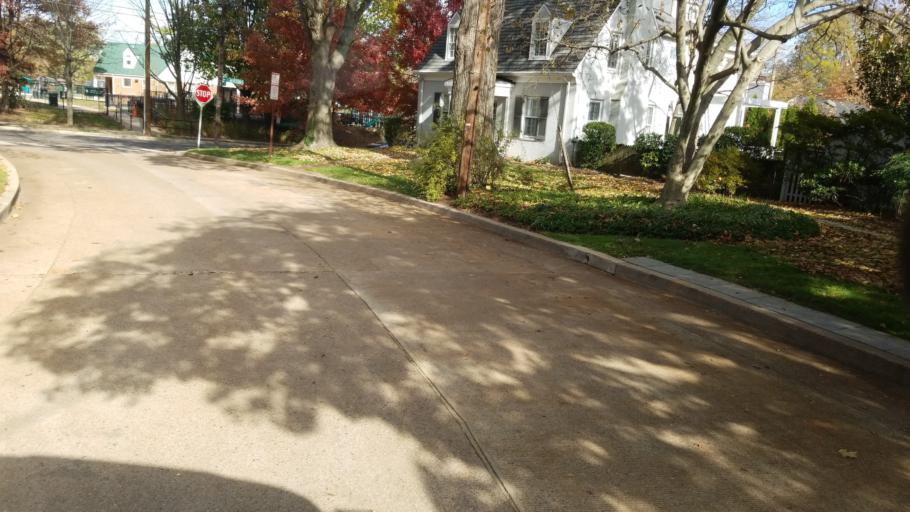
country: US
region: Maryland
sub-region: Montgomery County
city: Chevy Chase Village
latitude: 38.9627
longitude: -77.0812
